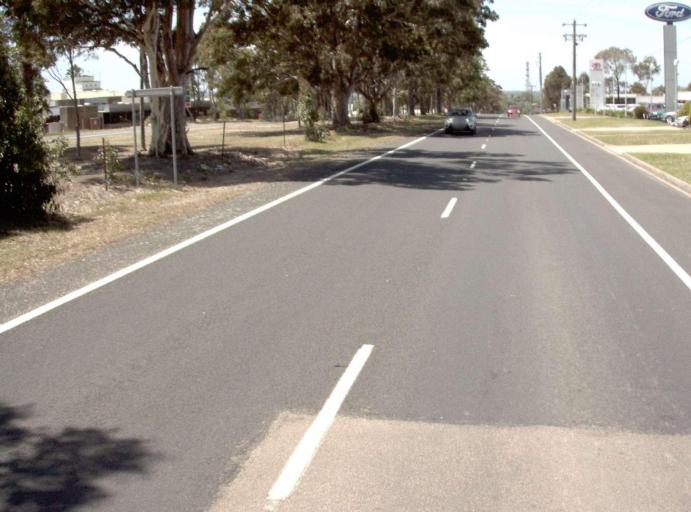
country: AU
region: Victoria
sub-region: East Gippsland
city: Bairnsdale
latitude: -37.8333
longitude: 147.6067
